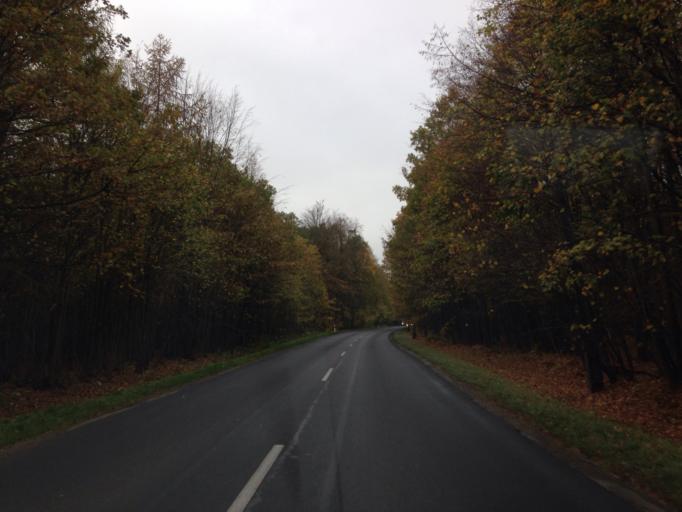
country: PL
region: Kujawsko-Pomorskie
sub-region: Powiat brodnicki
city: Brodnica
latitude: 53.2622
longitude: 19.3383
